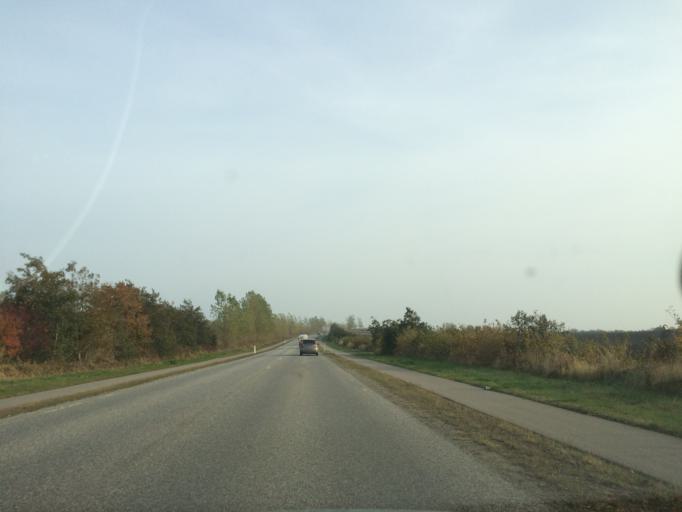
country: DK
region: Zealand
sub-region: Odsherred Kommune
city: Asnaes
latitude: 55.9761
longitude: 11.3372
